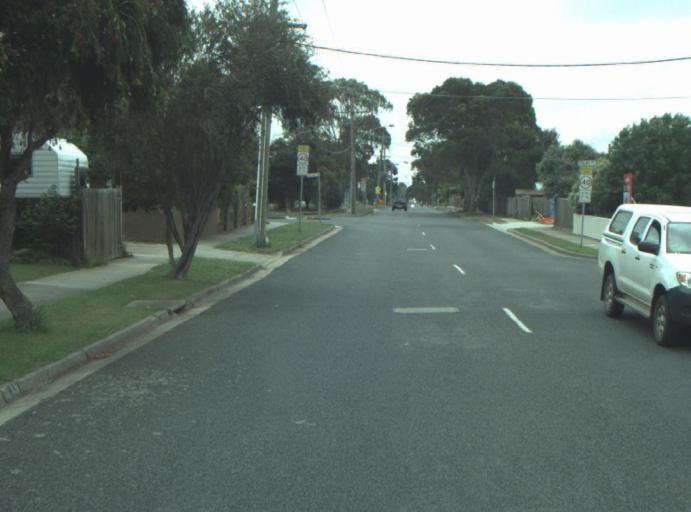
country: AU
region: Victoria
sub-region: Greater Geelong
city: Wandana Heights
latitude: -38.1869
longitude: 144.3252
